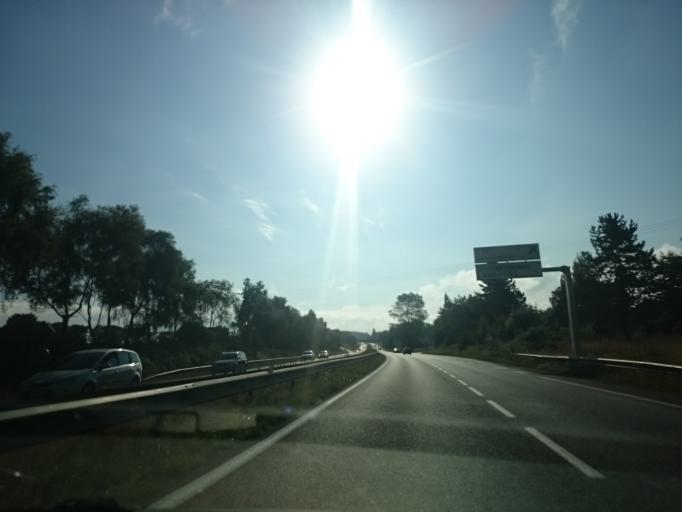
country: FR
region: Brittany
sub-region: Departement des Cotes-d'Armor
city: Lanrodec
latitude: 48.5361
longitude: -3.0521
